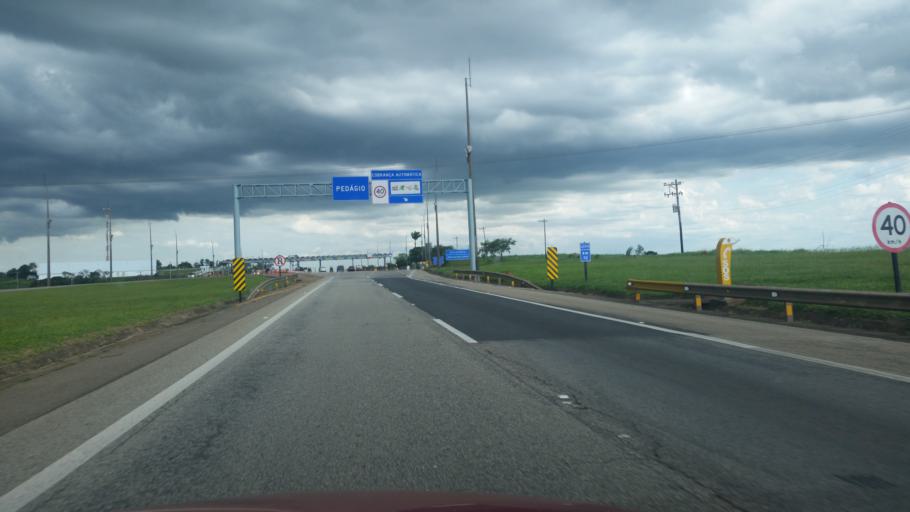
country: BR
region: Sao Paulo
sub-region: Boituva
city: Boituva
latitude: -23.3117
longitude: -47.6470
